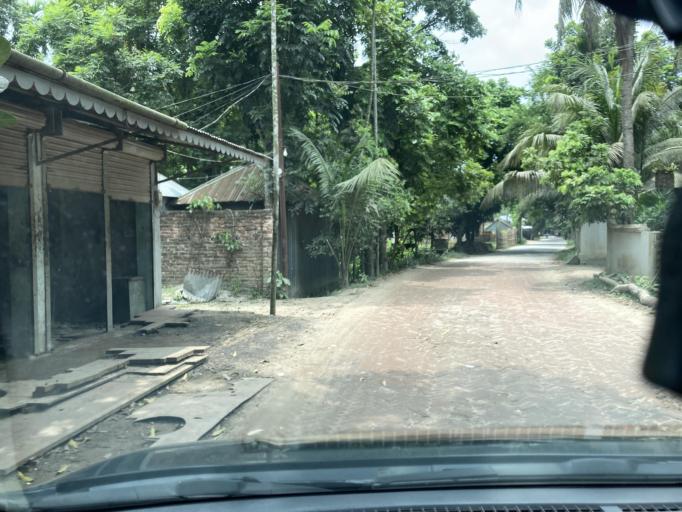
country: BD
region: Dhaka
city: Dohar
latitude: 23.8153
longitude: 90.0470
